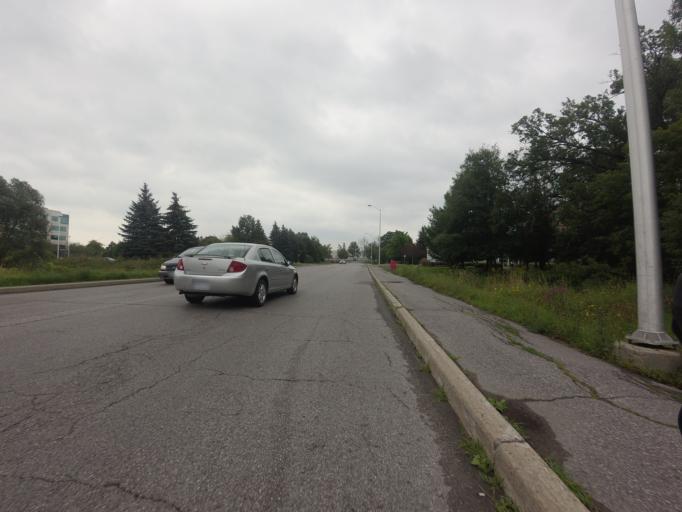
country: CA
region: Ontario
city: Bells Corners
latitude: 45.3425
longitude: -75.9203
